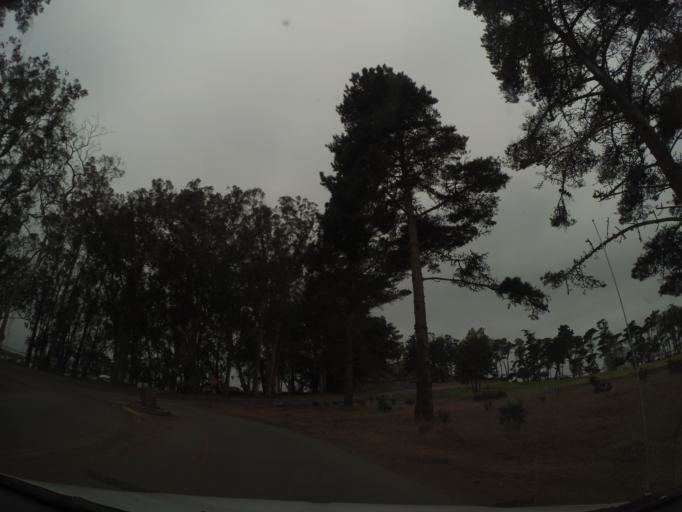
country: US
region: California
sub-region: San Luis Obispo County
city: Morro Bay
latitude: 35.3467
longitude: -120.8416
